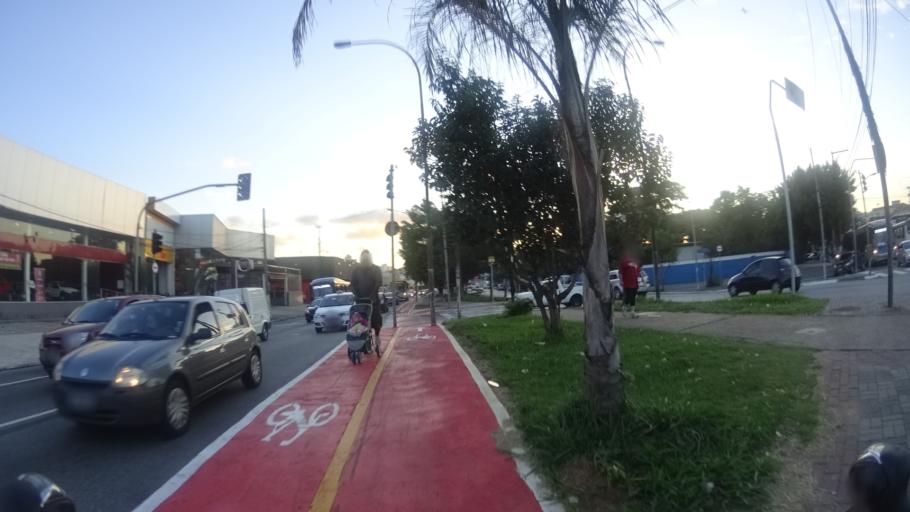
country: BR
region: Sao Paulo
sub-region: Sao Paulo
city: Sao Paulo
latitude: -23.4887
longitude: -46.6514
